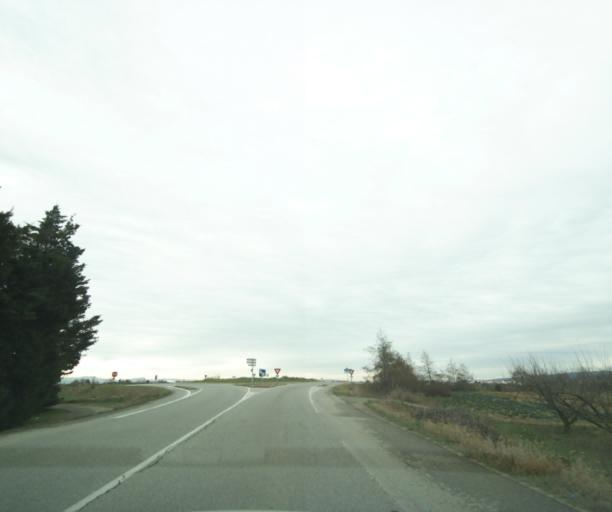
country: FR
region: Rhone-Alpes
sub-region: Departement de la Drome
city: Bourg-les-Valence
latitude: 44.9666
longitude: 4.9104
